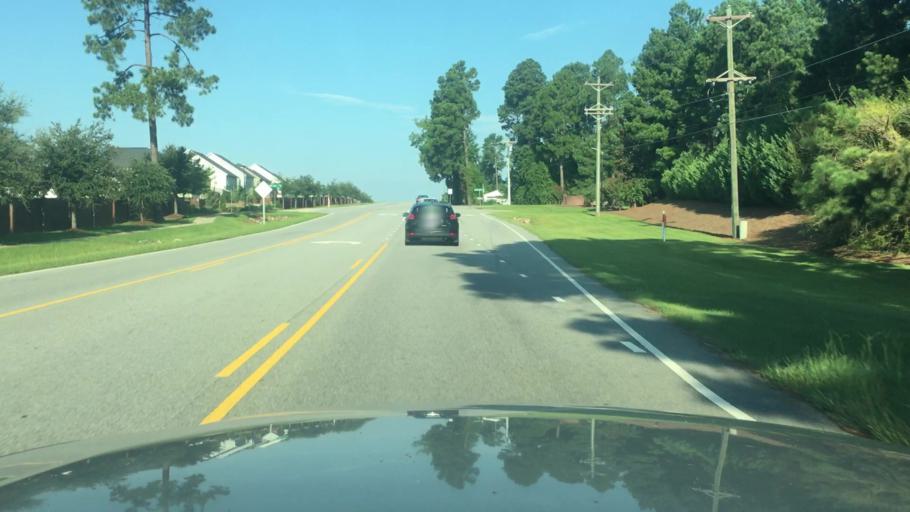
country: US
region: North Carolina
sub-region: Cumberland County
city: Spring Lake
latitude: 35.1550
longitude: -78.8944
